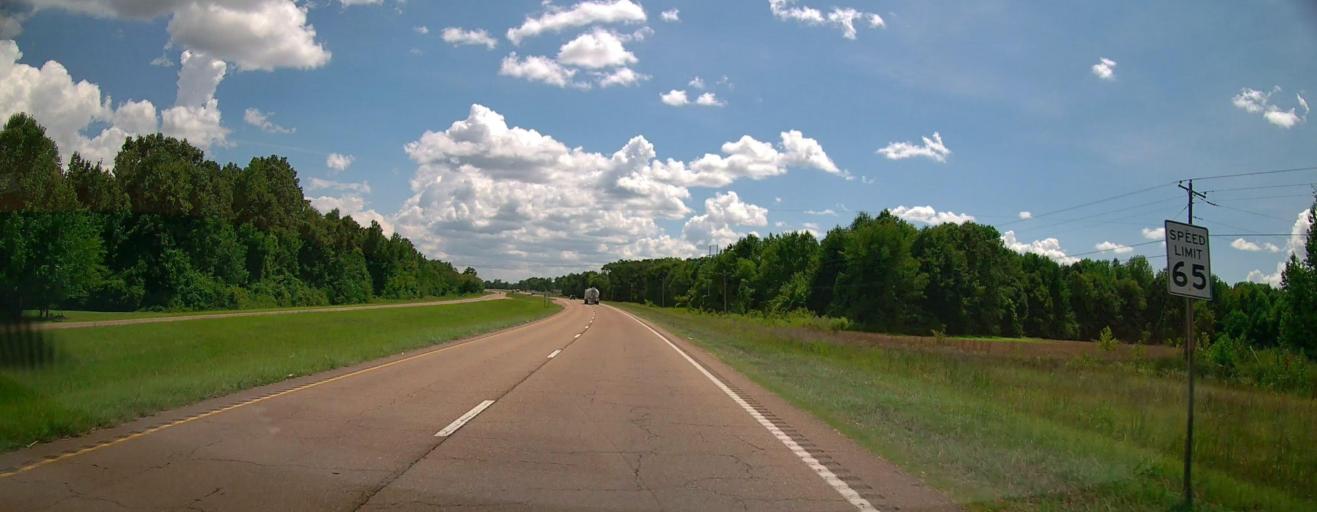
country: US
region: Mississippi
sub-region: Lowndes County
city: Columbus Air Force Base
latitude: 33.7224
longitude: -88.4481
